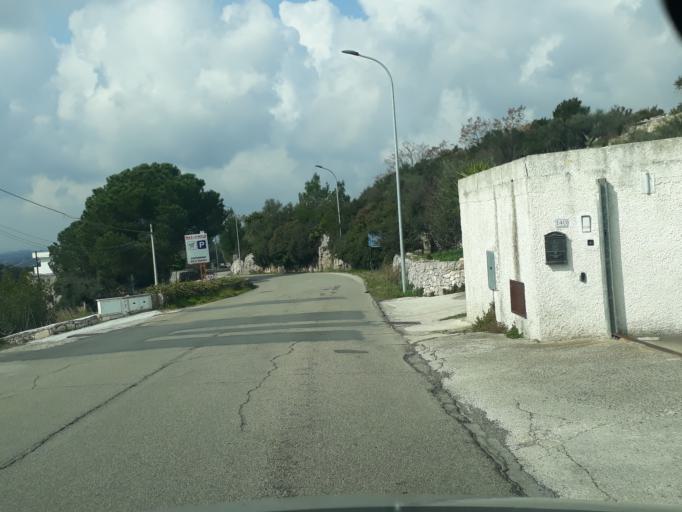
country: IT
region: Apulia
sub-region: Provincia di Brindisi
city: Cisternino
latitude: 40.7445
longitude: 17.4168
